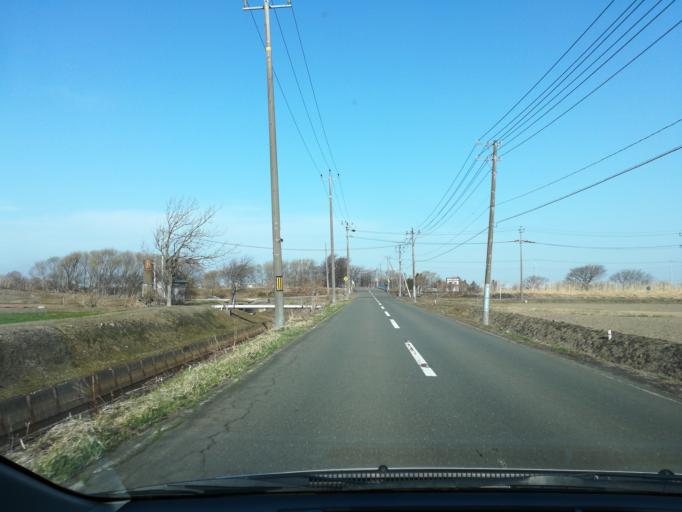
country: JP
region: Hokkaido
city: Ebetsu
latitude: 43.1552
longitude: 141.6422
